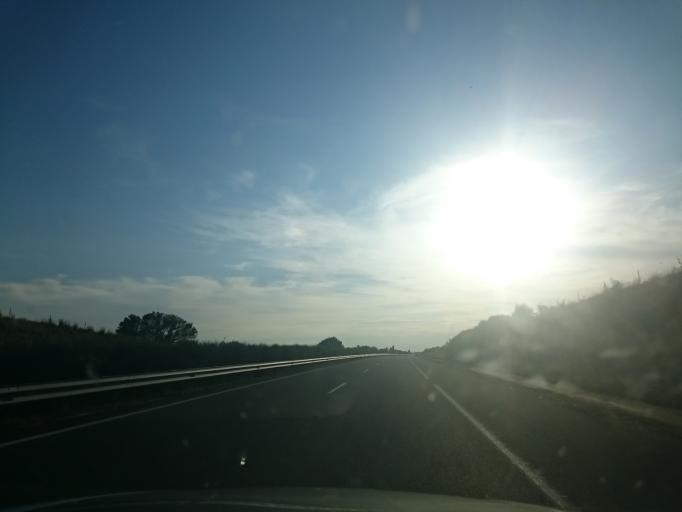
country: ES
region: Castille and Leon
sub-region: Provincia de Palencia
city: Moratinos
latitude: 42.3635
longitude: -4.9276
